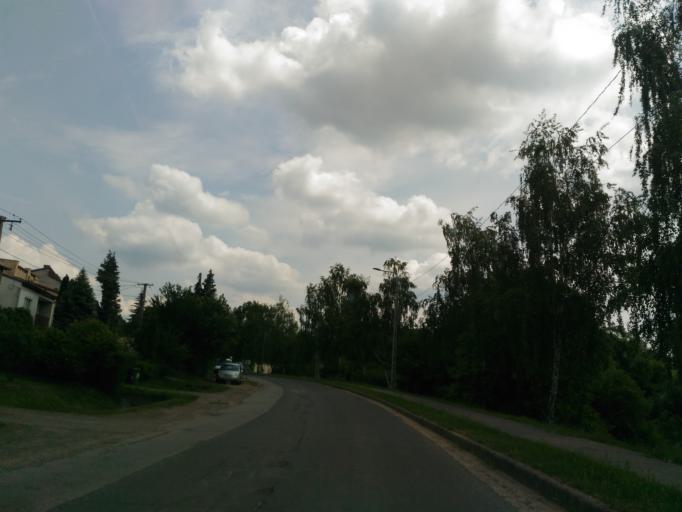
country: HU
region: Baranya
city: Komlo
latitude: 46.1885
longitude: 18.2378
